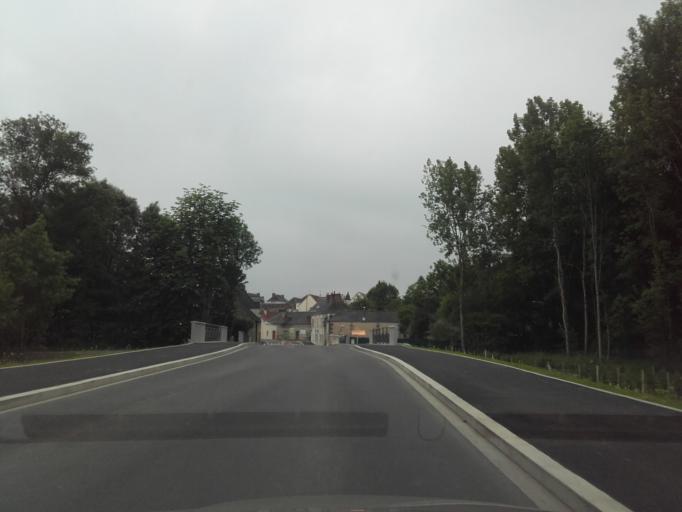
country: FR
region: Centre
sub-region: Departement d'Indre-et-Loire
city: Cerelles
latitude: 47.4938
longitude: 0.6958
